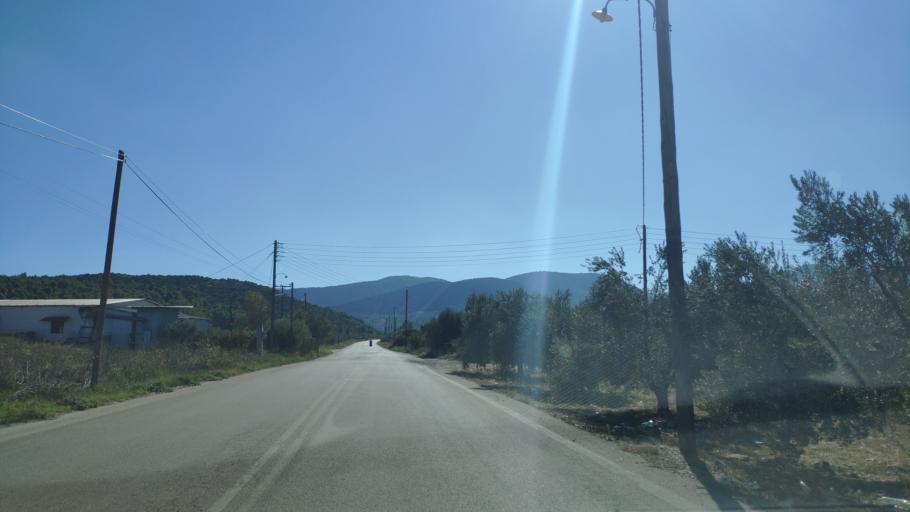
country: GR
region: Peloponnese
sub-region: Nomos Korinthias
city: Athikia
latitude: 37.8358
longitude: 22.9135
